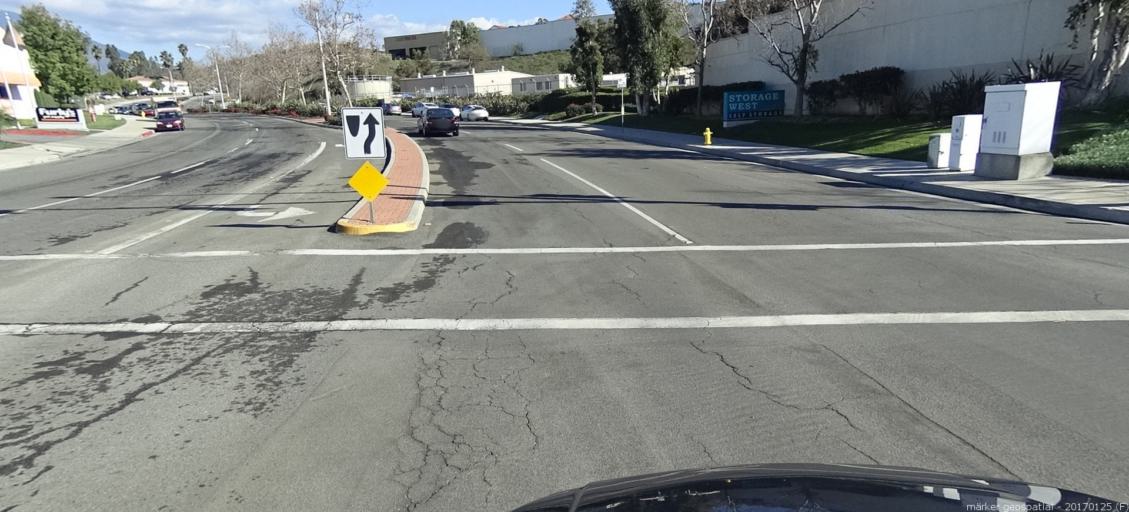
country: US
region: California
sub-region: Orange County
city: Lake Forest
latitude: 33.6614
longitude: -117.6714
